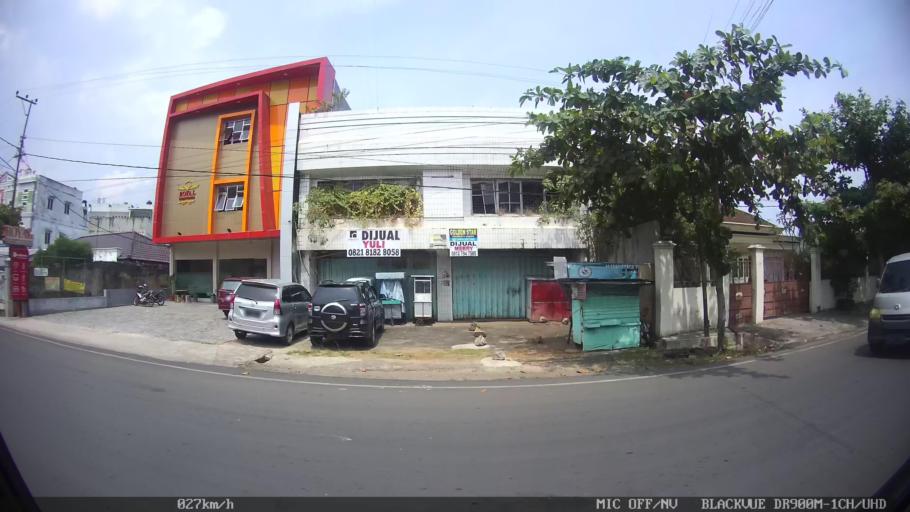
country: ID
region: Lampung
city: Bandarlampung
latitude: -5.4412
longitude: 105.2653
